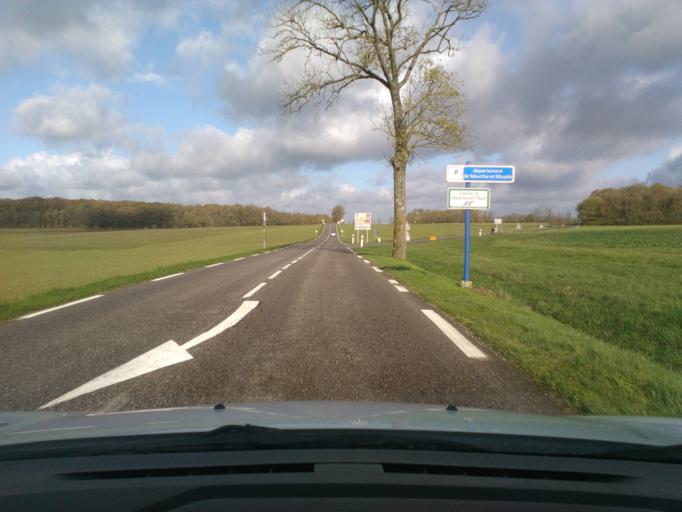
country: FR
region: Lorraine
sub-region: Departement des Vosges
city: Mirecourt
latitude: 48.3645
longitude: 6.1227
